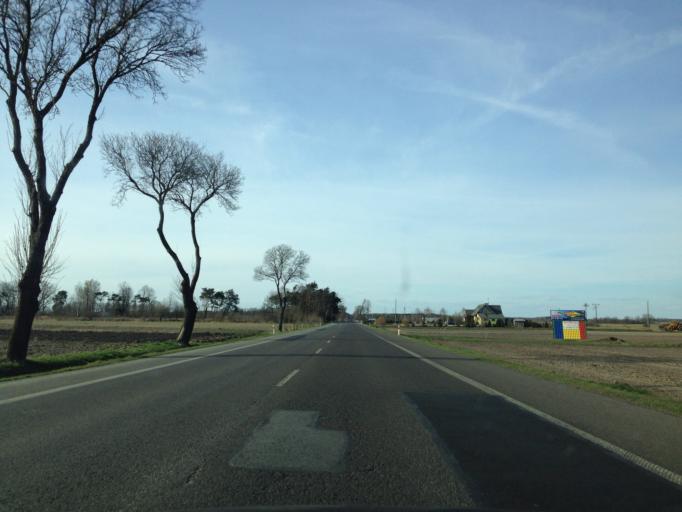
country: PL
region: Lodz Voivodeship
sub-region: Powiat kutnowski
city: Ostrowy
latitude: 52.3292
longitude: 19.1507
